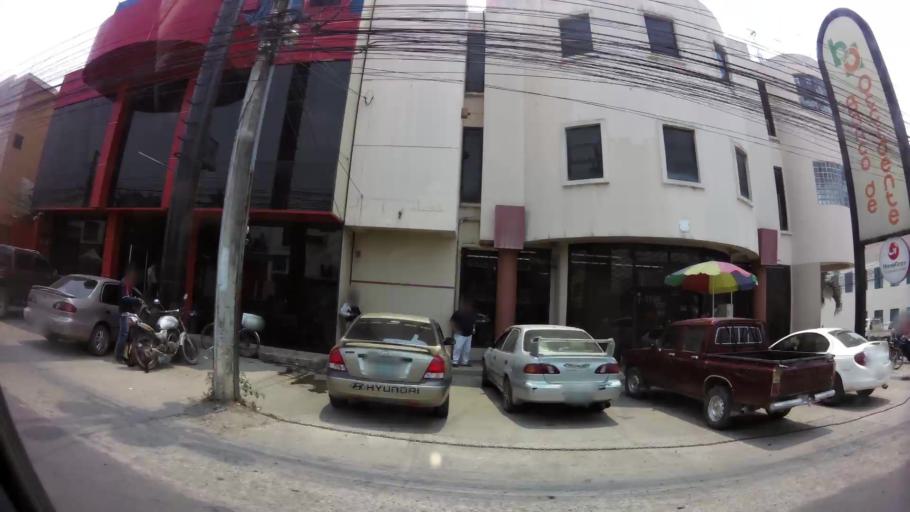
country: HN
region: Yoro
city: El Progreso
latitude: 15.4022
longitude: -87.8055
